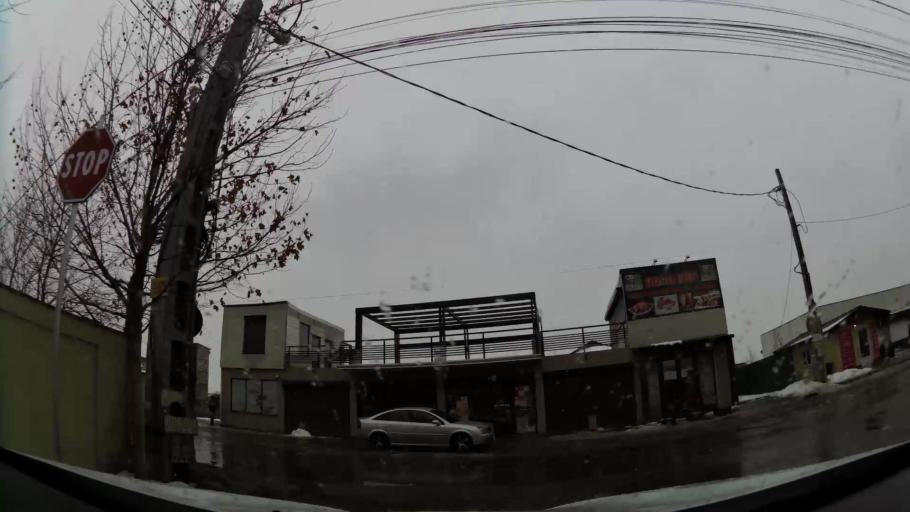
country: RO
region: Ilfov
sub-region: Comuna Bragadiru
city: Bragadiru
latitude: 44.3982
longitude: 26.0037
